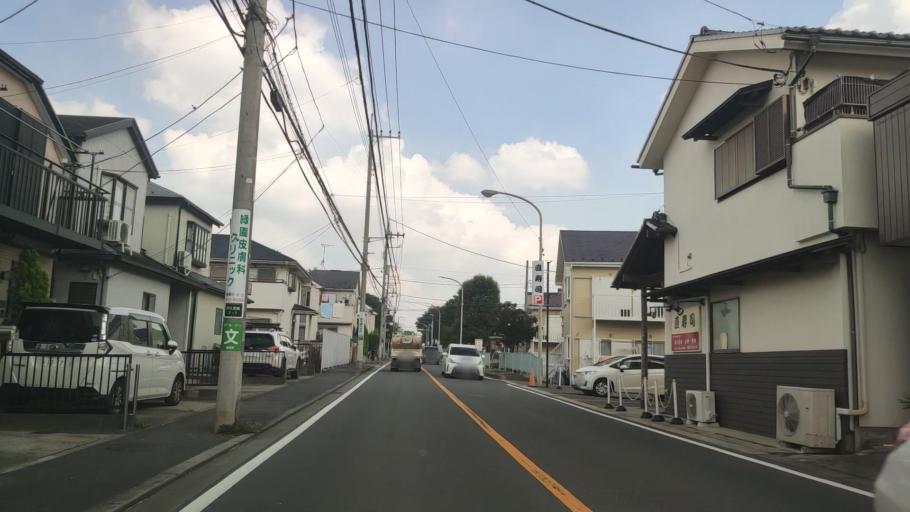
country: JP
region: Kanagawa
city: Minami-rinkan
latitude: 35.4532
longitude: 139.5023
